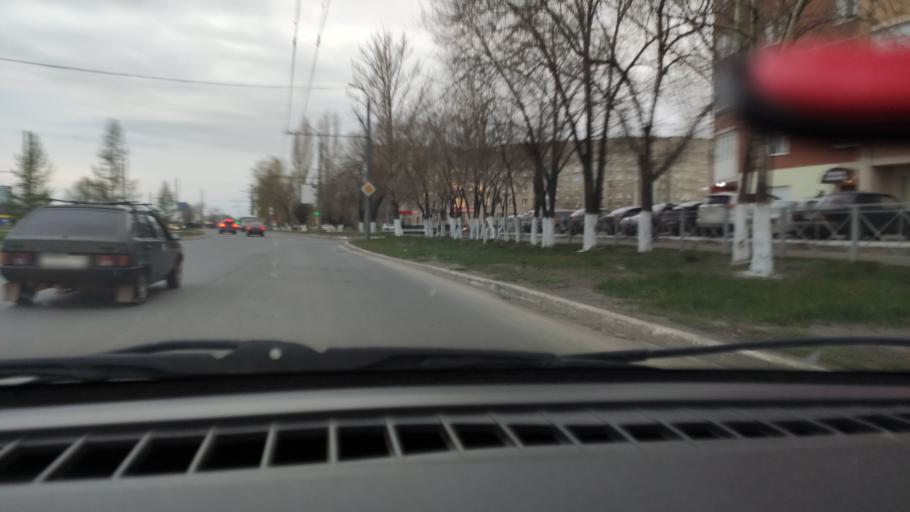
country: RU
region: Orenburg
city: Orenburg
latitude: 51.8166
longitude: 55.1073
